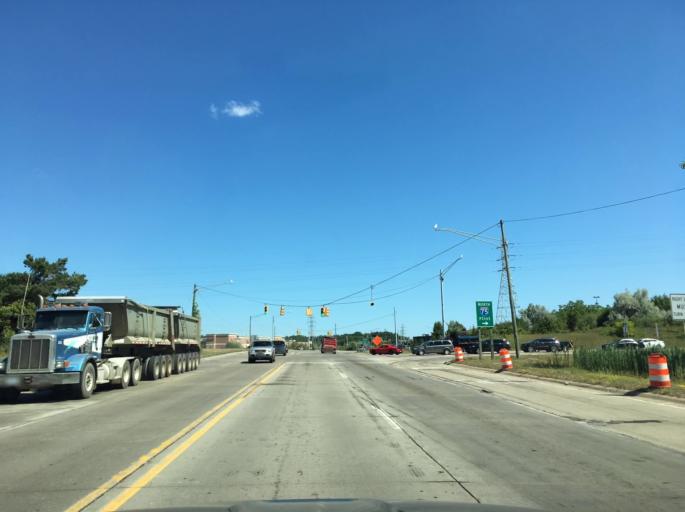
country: US
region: Michigan
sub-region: Oakland County
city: Auburn Hills
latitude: 42.7020
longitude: -83.2843
